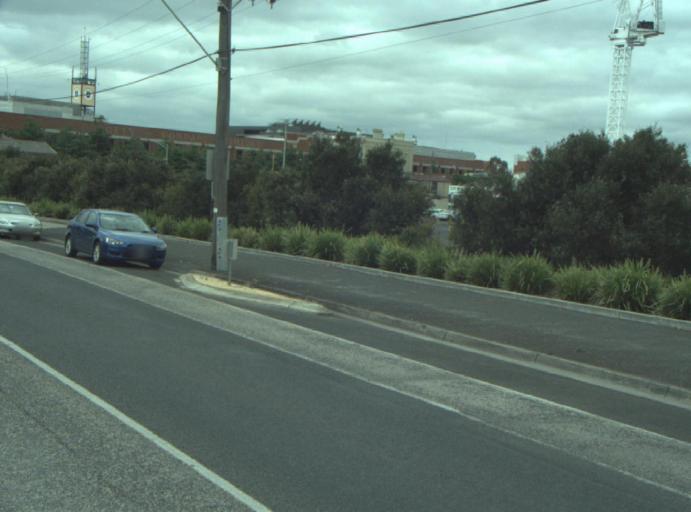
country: AU
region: Victoria
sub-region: Greater Geelong
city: Geelong
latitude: -38.1419
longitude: 144.3587
